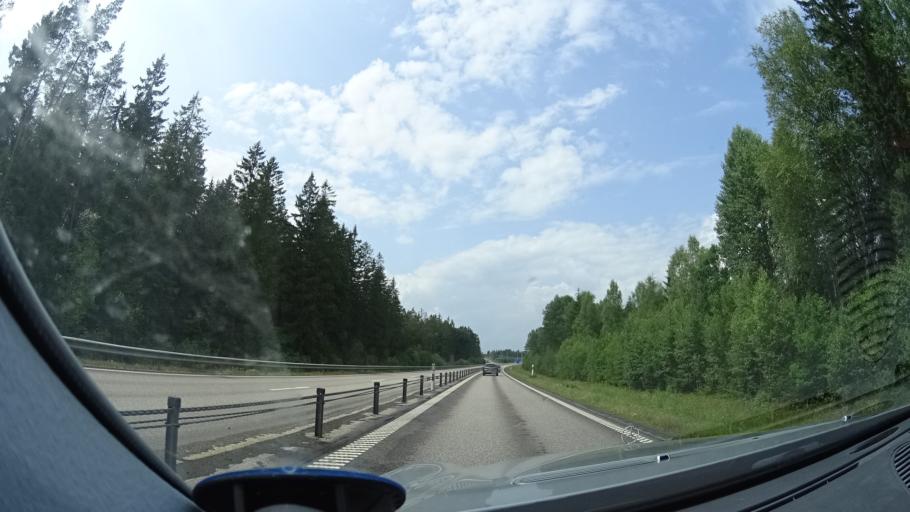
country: SE
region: Kalmar
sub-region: Nybro Kommun
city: Nybro
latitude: 56.7263
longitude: 15.8966
